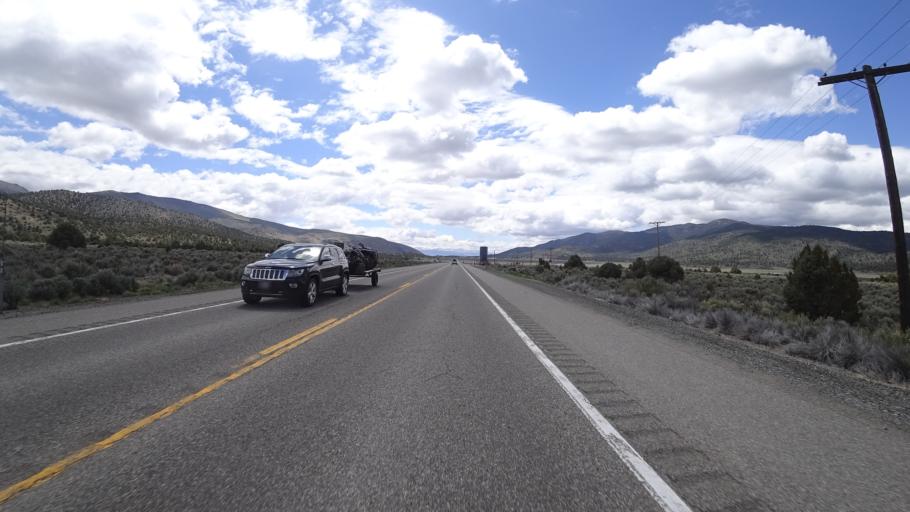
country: US
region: Nevada
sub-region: Douglas County
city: Gardnerville Ranchos
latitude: 38.8052
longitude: -119.6078
